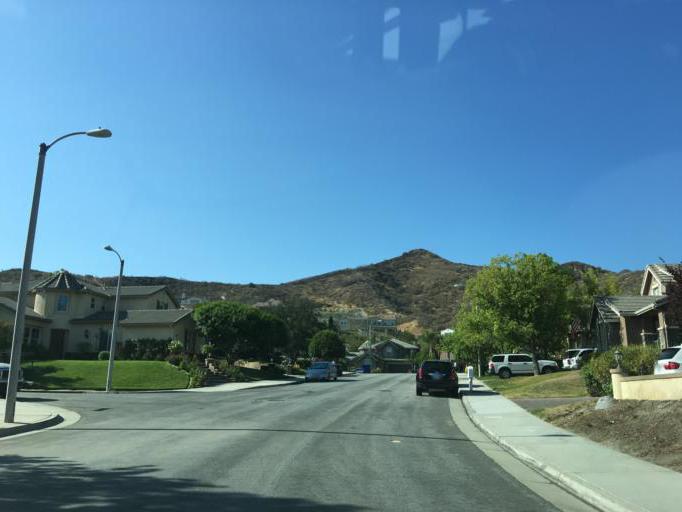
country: US
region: California
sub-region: Los Angeles County
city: Santa Clarita
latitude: 34.3758
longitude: -118.5882
